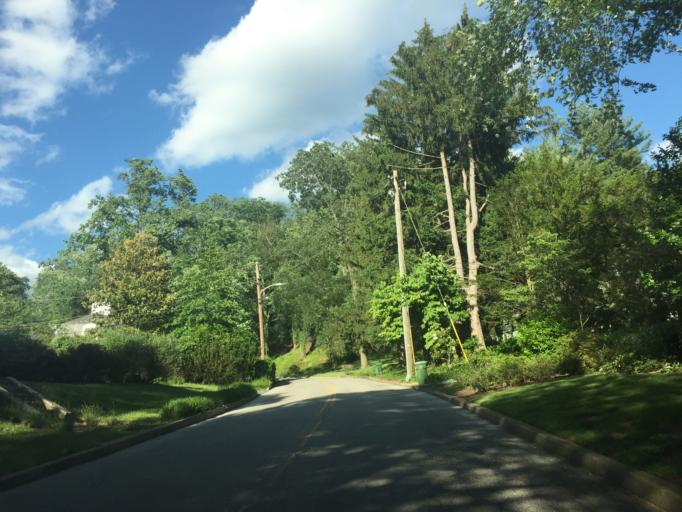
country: US
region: Maryland
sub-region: Baltimore County
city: Towson
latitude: 39.3688
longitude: -76.6471
